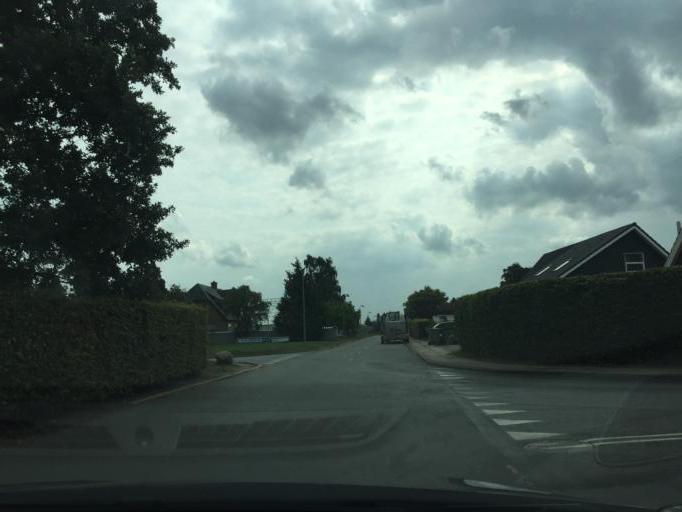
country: DK
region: South Denmark
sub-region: Odense Kommune
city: Stige
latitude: 55.4436
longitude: 10.4048
